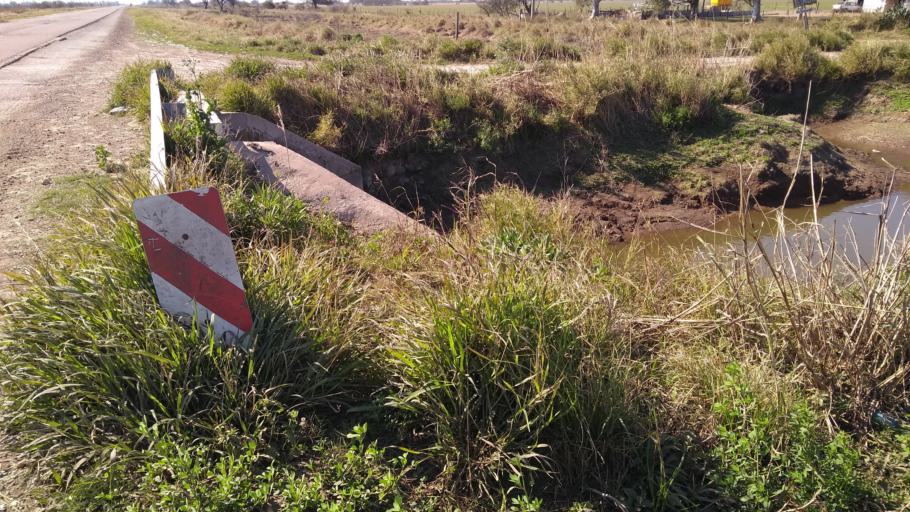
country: AR
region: Santiago del Estero
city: Los Juries
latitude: -28.5978
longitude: -61.5165
